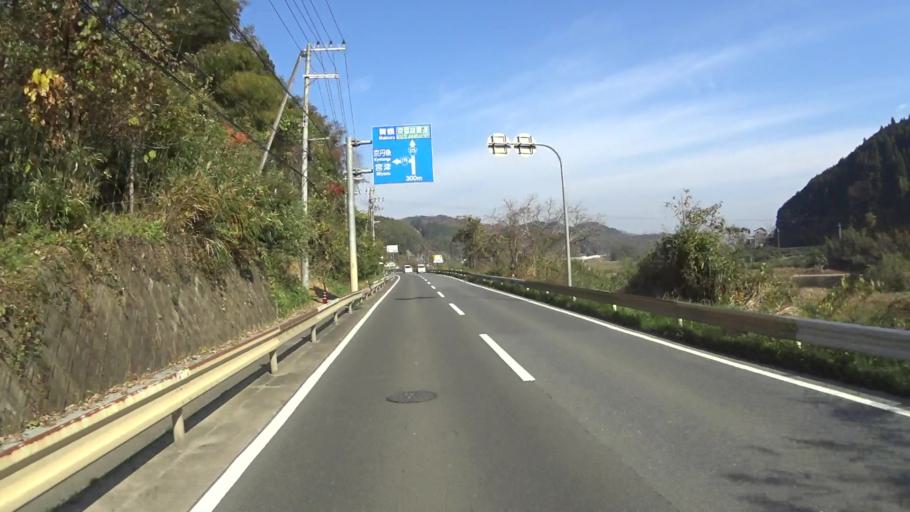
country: JP
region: Kyoto
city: Fukuchiyama
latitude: 35.3603
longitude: 135.1140
